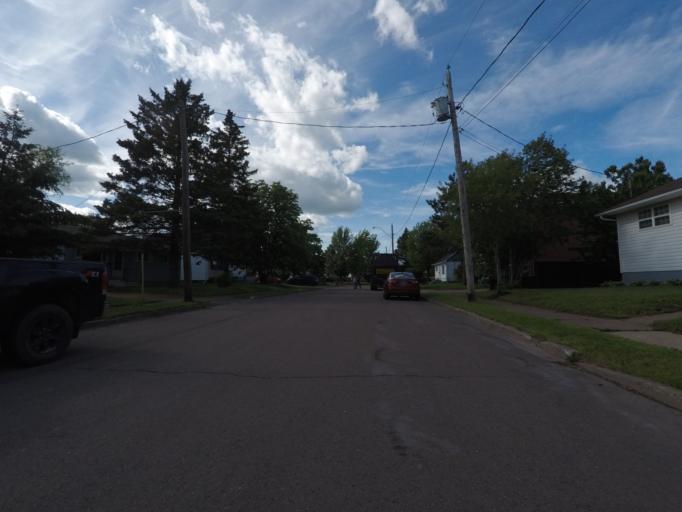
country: CA
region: New Brunswick
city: Moncton
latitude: 46.0957
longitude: -64.8254
